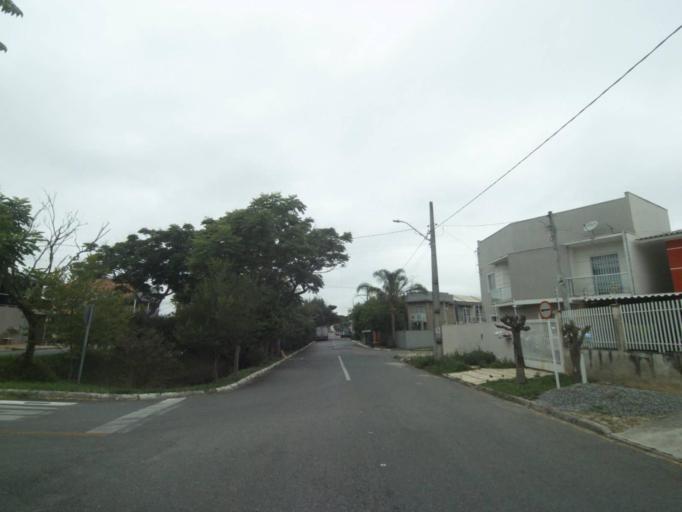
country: BR
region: Parana
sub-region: Araucaria
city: Araucaria
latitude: -25.5436
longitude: -49.3443
